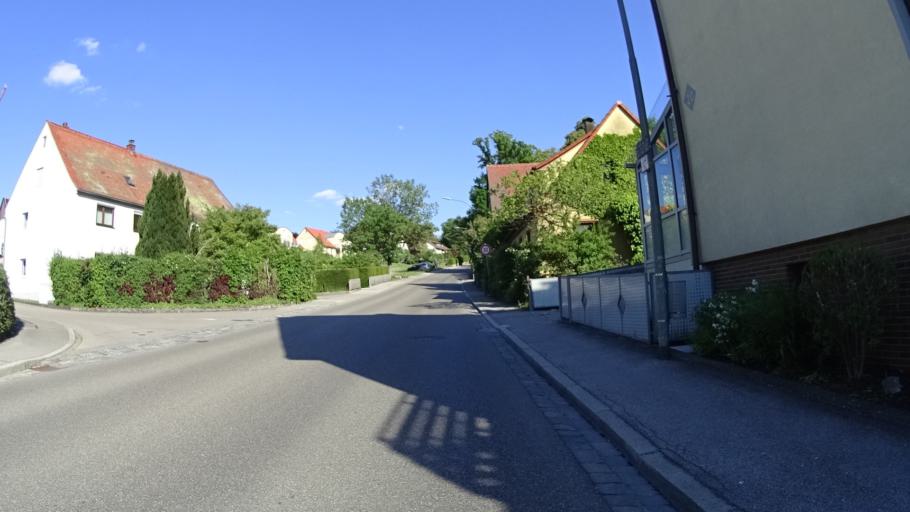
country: DE
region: Bavaria
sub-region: Regierungsbezirk Mittelfranken
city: Feuchtwangen
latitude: 49.1657
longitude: 10.3375
